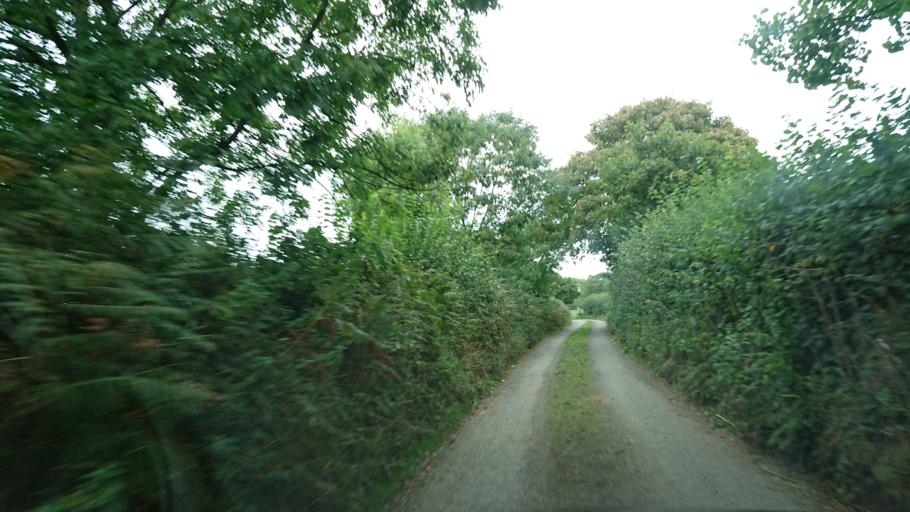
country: IE
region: Munster
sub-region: Waterford
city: Dunmore East
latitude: 52.2006
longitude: -7.0461
